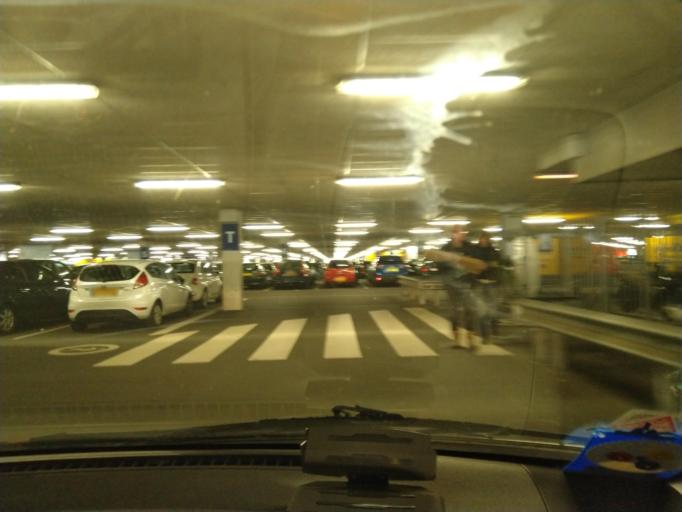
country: NL
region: Groningen
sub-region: Gemeente Groningen
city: Oosterpark
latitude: 53.2171
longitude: 6.5904
